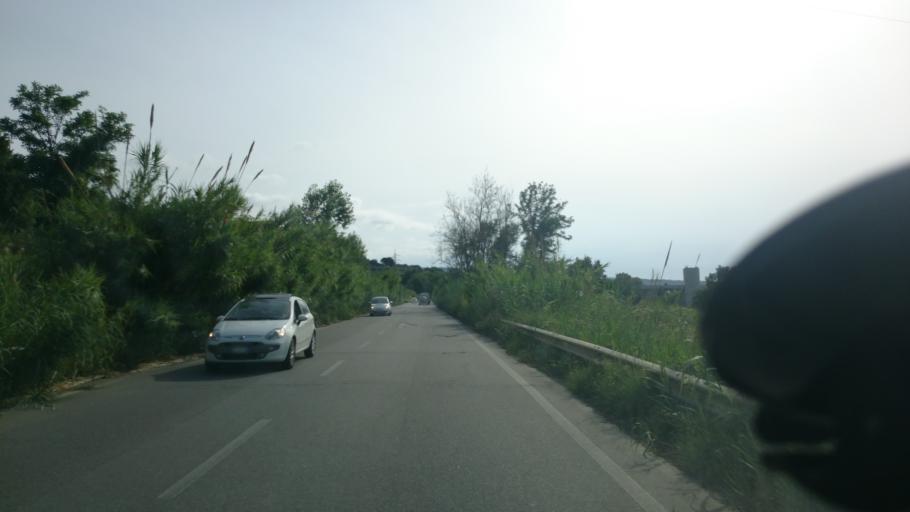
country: IT
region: Calabria
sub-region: Provincia di Vibo-Valentia
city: Sant'Onofrio
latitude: 38.7090
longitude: 16.1198
